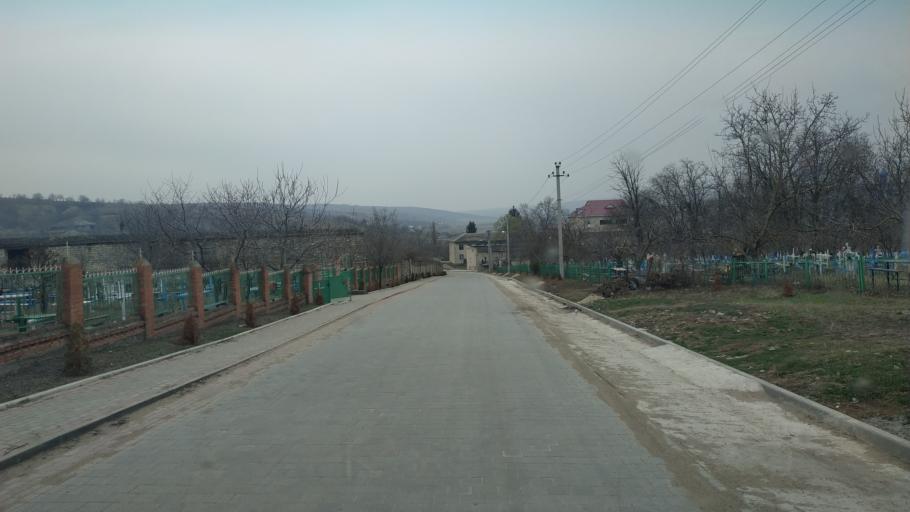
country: MD
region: Chisinau
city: Singera
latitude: 46.8255
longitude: 29.0409
